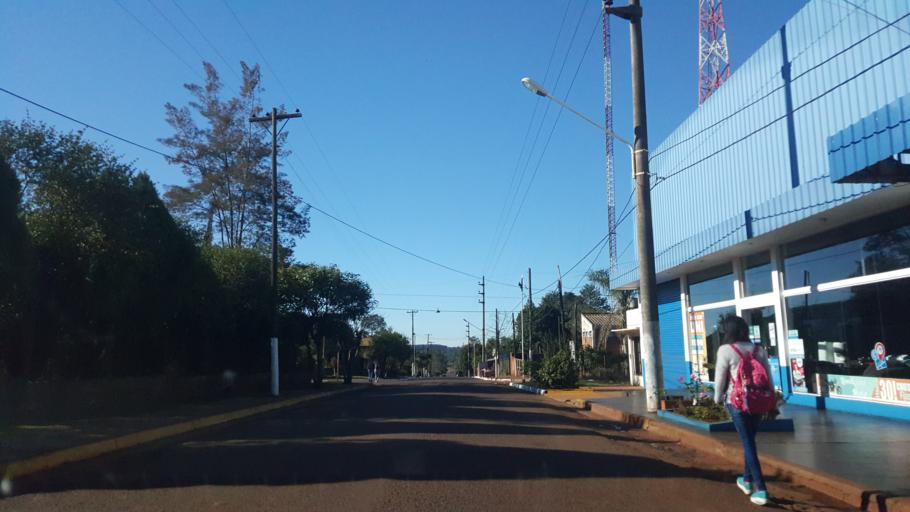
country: AR
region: Misiones
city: Gobernador Roca
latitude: -27.1890
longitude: -55.4659
